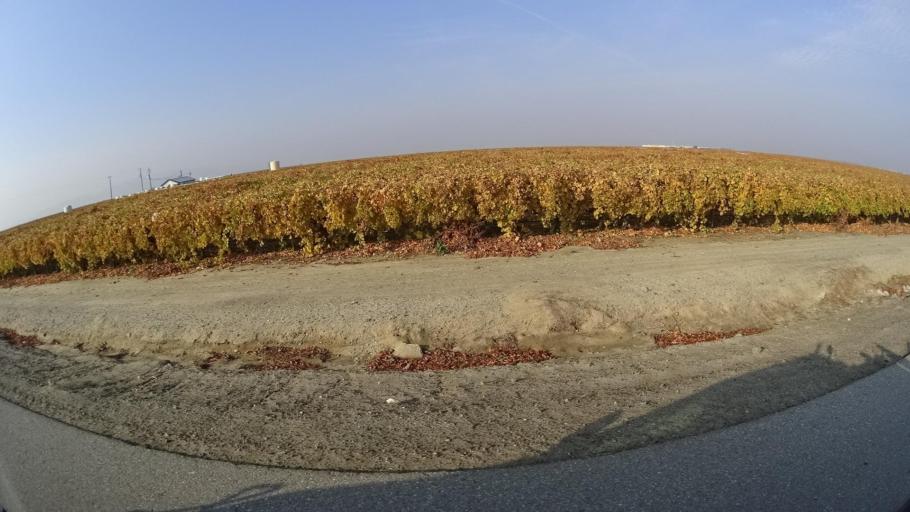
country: US
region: California
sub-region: Kern County
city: Arvin
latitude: 35.0684
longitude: -118.9175
